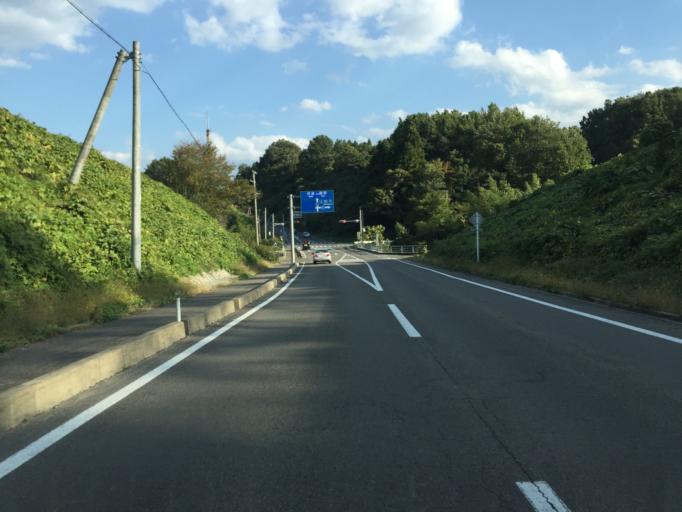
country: JP
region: Fukushima
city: Fukushima-shi
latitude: 37.6723
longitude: 140.5131
